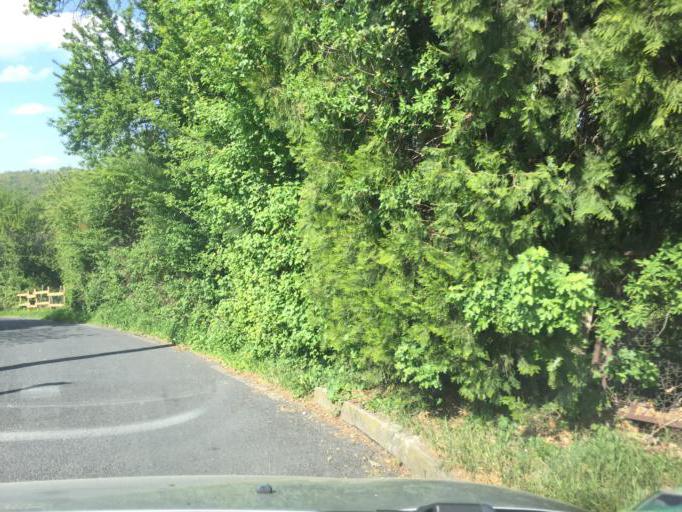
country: FR
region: Rhone-Alpes
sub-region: Departement du Rhone
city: Sathonay-Camp
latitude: 45.8281
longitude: 4.8726
